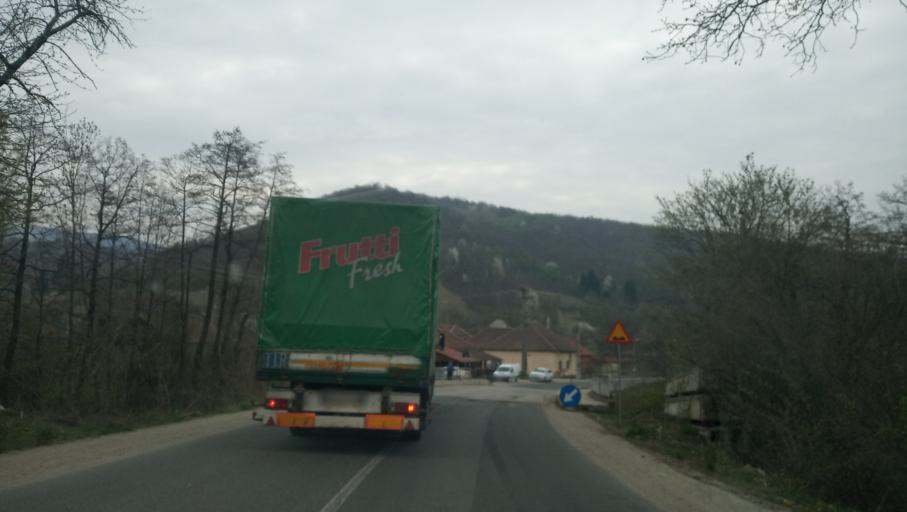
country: RO
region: Arad
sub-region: Comuna Varfurile
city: Varfurile
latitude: 46.3426
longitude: 22.5581
